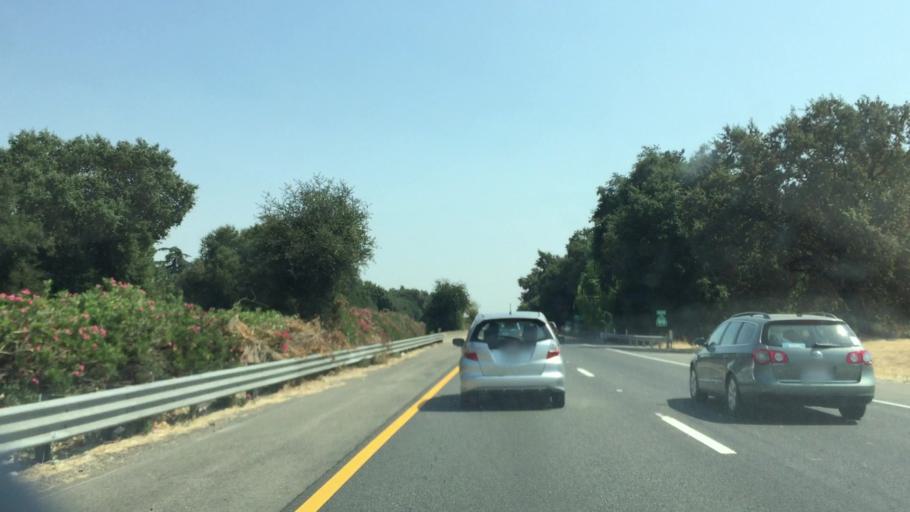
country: US
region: California
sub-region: Sacramento County
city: Galt
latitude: 38.2464
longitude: -121.2886
